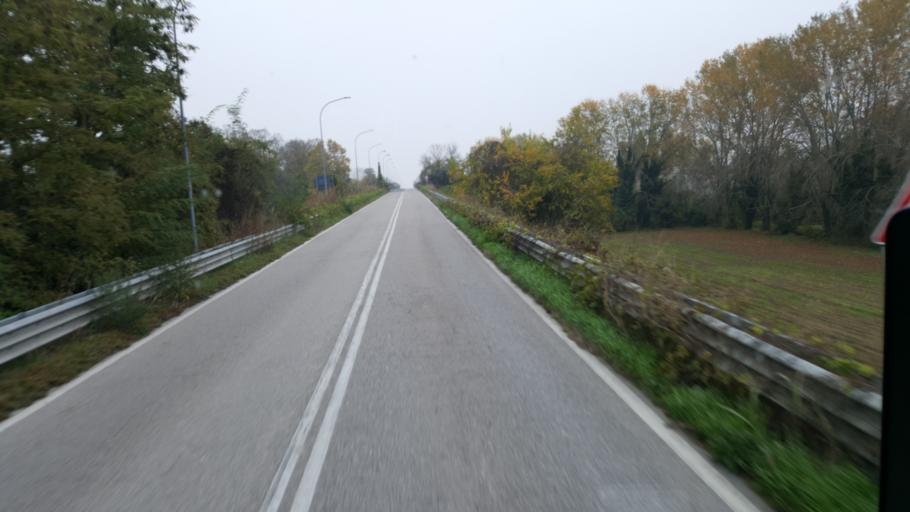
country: IT
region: Veneto
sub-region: Provincia di Rovigo
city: Ficarolo
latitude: 44.9458
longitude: 11.4193
